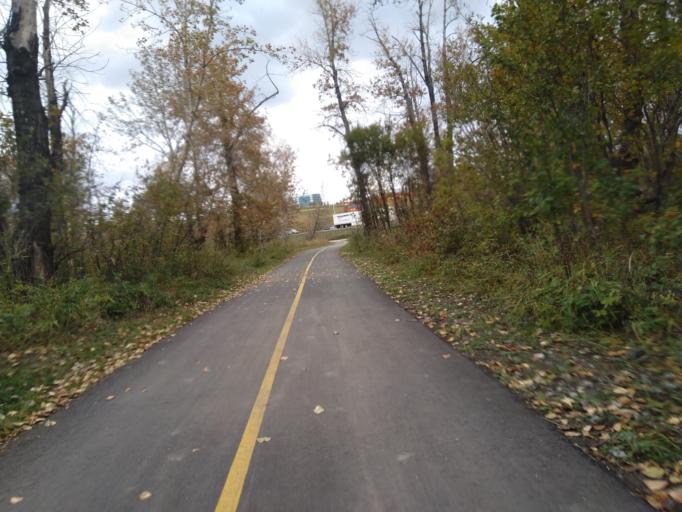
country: CA
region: Alberta
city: Calgary
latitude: 51.0398
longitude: -114.0087
